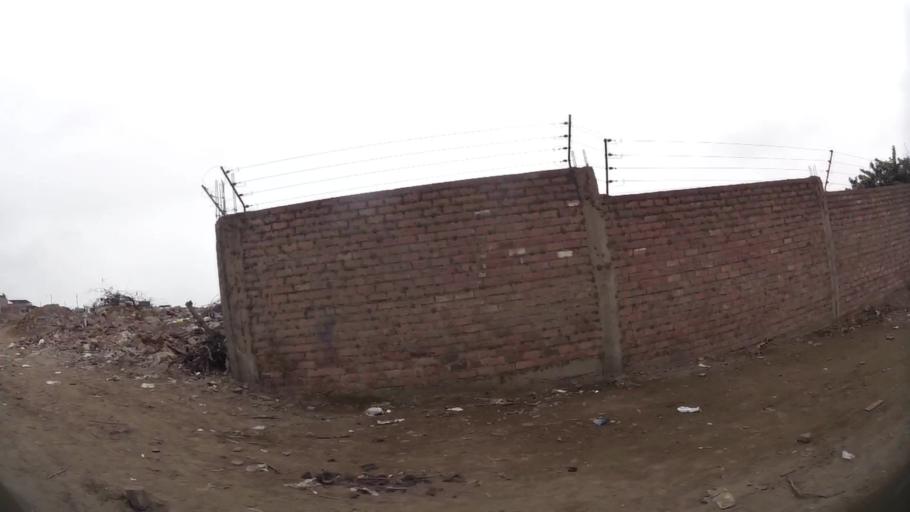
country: PE
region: Lima
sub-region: Lima
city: Cieneguilla
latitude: -12.2179
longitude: -76.9039
